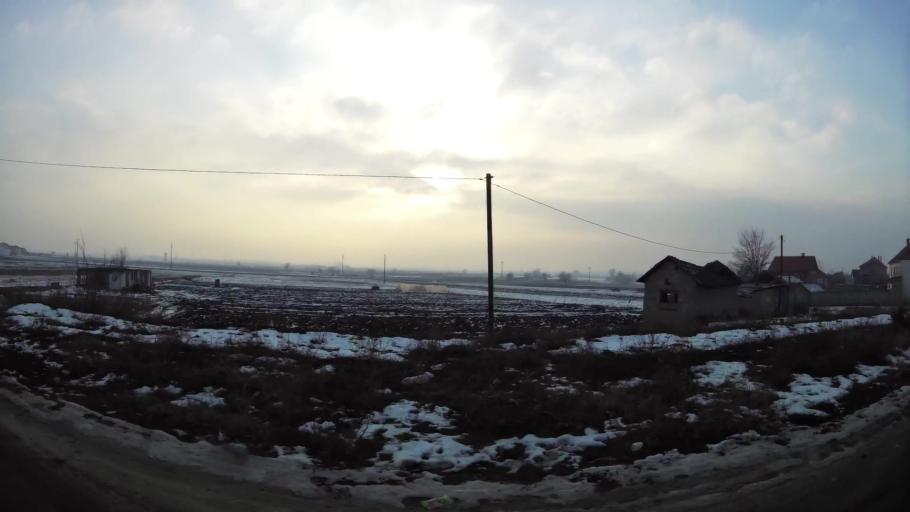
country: MK
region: Aracinovo
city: Arachinovo
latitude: 42.0232
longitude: 21.5581
